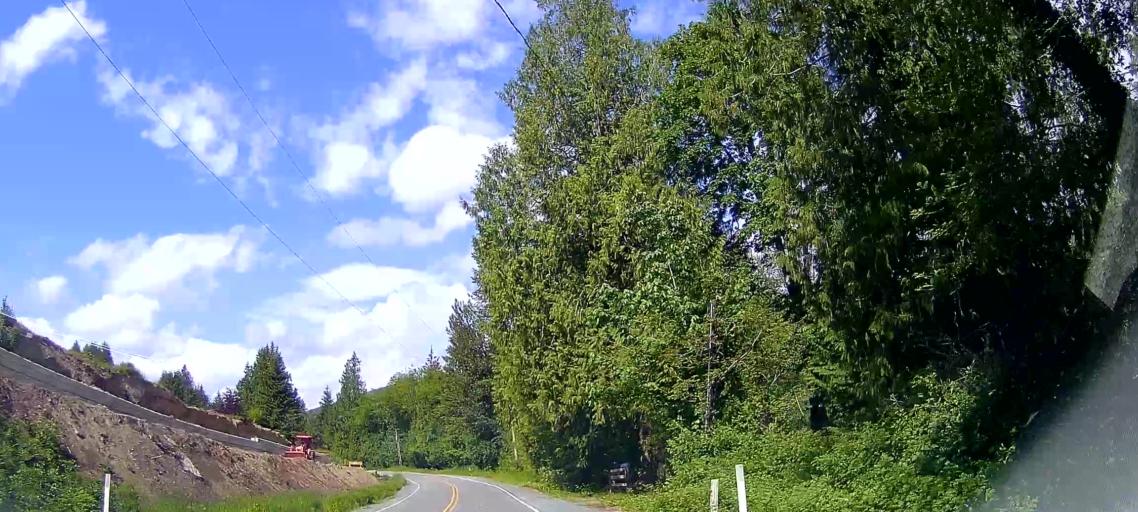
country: US
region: Washington
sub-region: Skagit County
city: Sedro-Woolley
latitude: 48.5539
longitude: -122.2119
